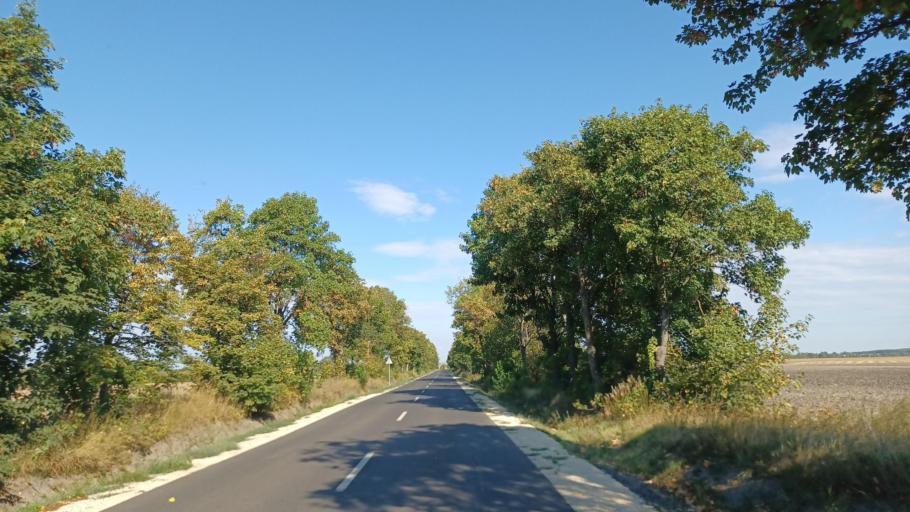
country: HU
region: Tolna
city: Dunaszentgyorgy
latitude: 46.4995
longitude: 18.8278
